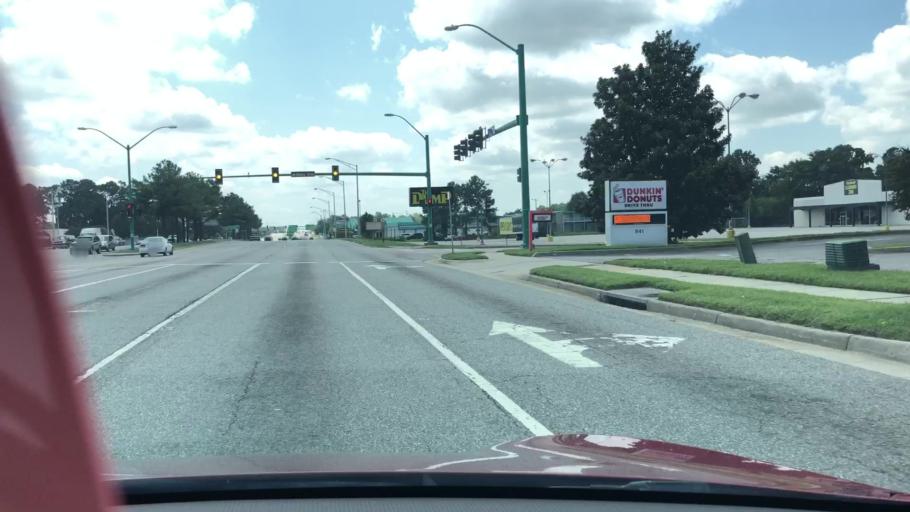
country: US
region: Virginia
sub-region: City of Chesapeake
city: Chesapeake
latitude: 36.8522
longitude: -76.2102
